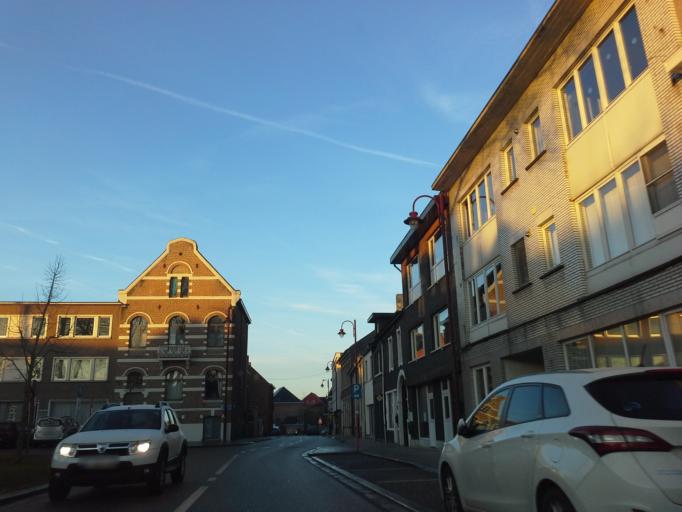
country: BE
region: Flanders
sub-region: Provincie Vlaams-Brabant
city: Scherpenheuvel-Zichem
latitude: 51.0018
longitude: 4.9868
